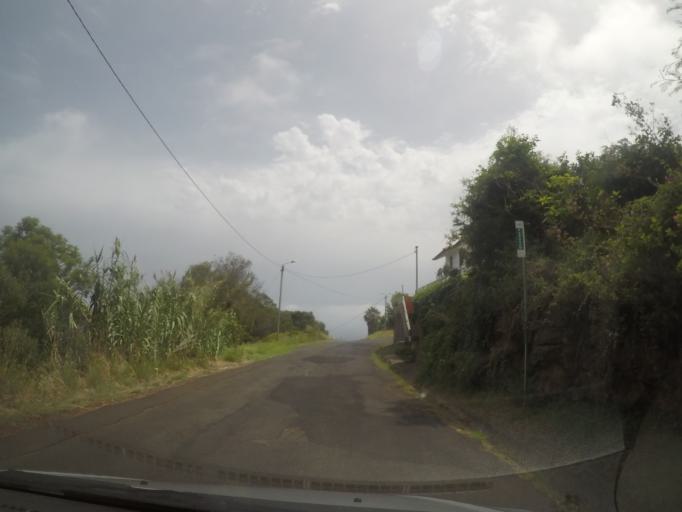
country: PT
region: Madeira
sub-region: Machico
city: Machico
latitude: 32.7024
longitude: -16.7865
